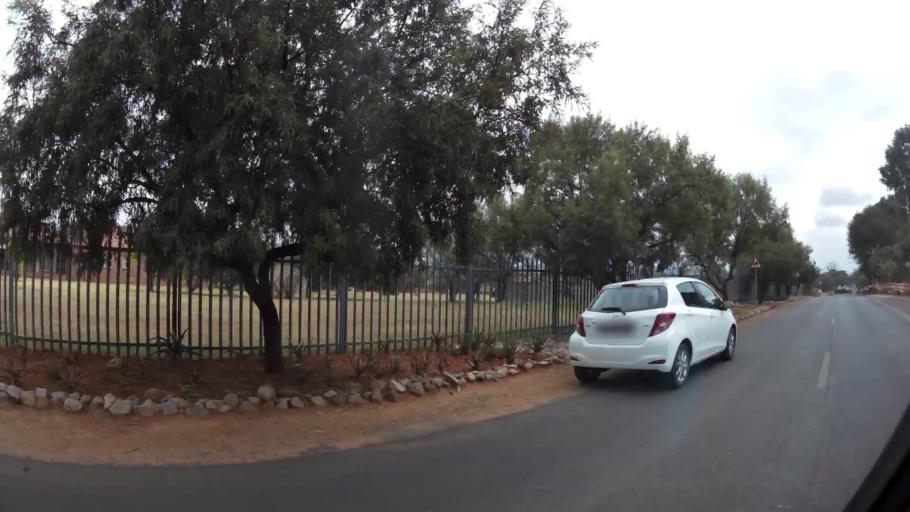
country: ZA
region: Gauteng
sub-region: West Rand District Municipality
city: Muldersdriseloop
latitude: -26.0892
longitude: 27.8733
